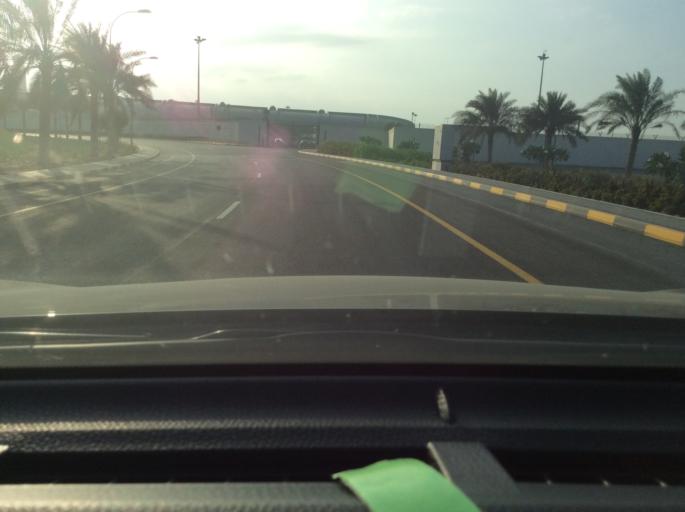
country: OM
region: Muhafazat Masqat
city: Bawshar
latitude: 23.6049
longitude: 58.2913
